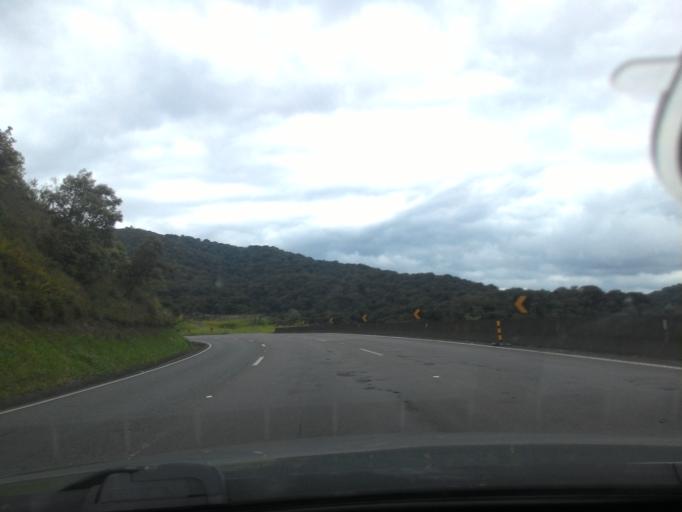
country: BR
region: Sao Paulo
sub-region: Cajati
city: Cajati
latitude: -24.9489
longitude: -48.4236
